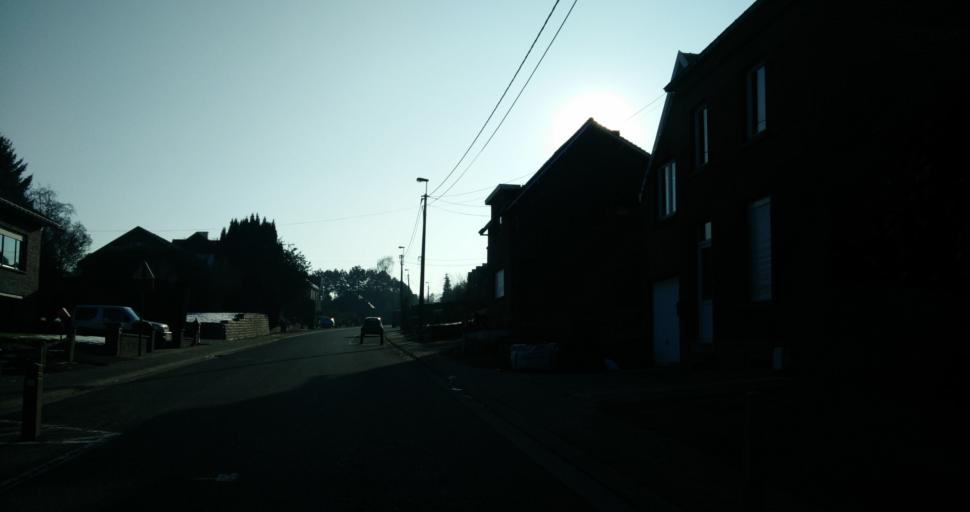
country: BE
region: Wallonia
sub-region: Province du Brabant Wallon
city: Braine-le-Chateau
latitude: 50.6791
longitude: 4.2674
